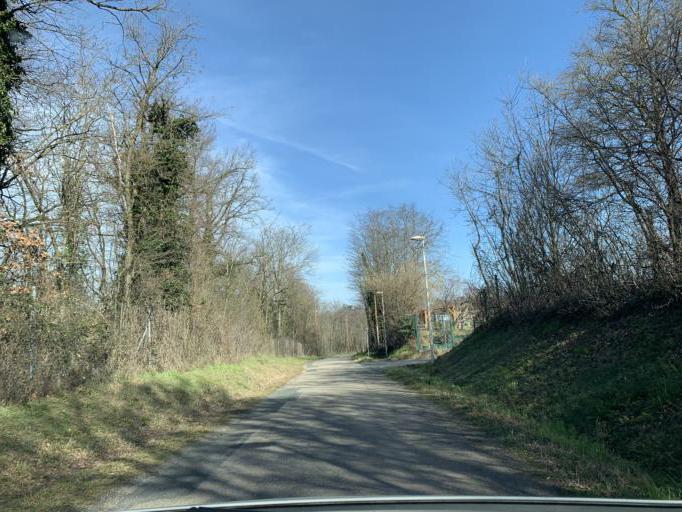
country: FR
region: Rhone-Alpes
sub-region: Departement du Rhone
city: Rillieux-la-Pape
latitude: 45.8131
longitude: 4.9187
